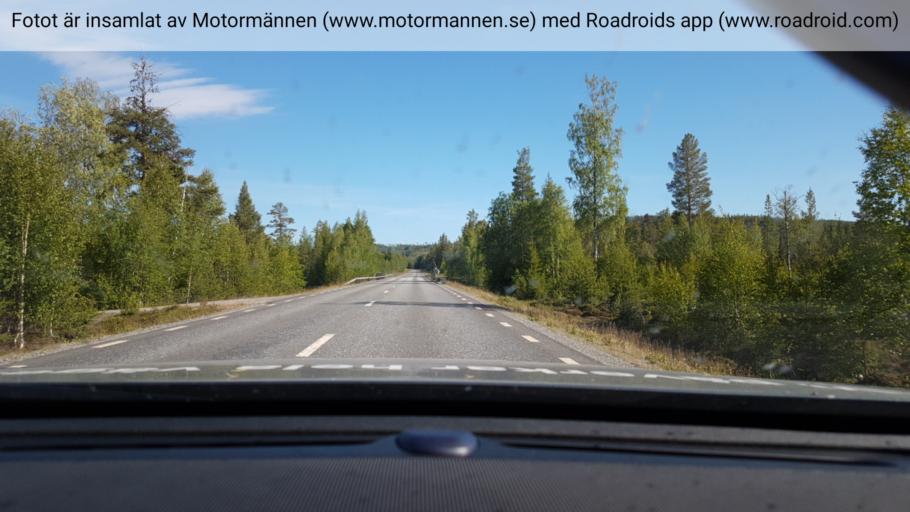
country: SE
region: Vaesterbotten
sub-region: Lycksele Kommun
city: Soderfors
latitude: 64.7258
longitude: 18.2232
